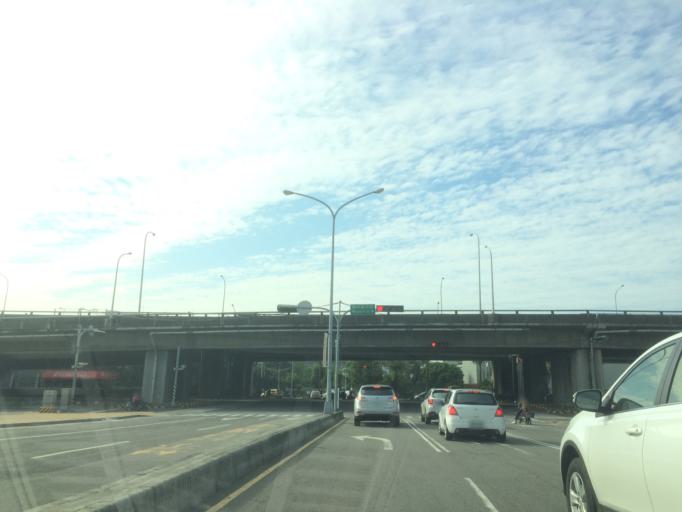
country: TW
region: Taiwan
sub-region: Taichung City
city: Taichung
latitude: 24.1522
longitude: 120.6246
